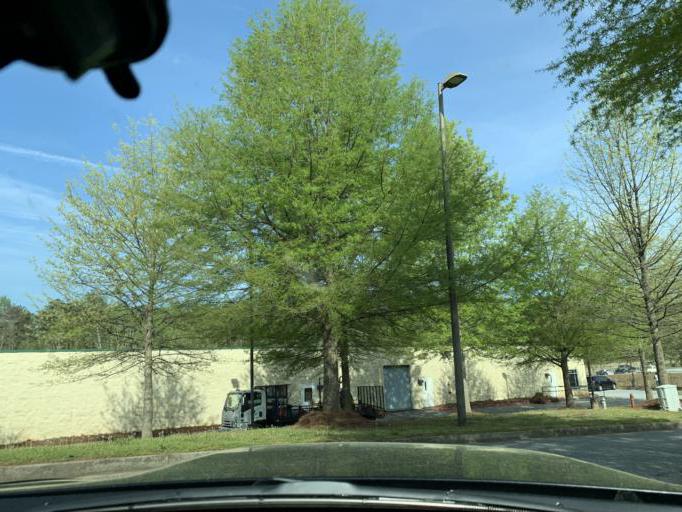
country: US
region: Georgia
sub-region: Forsyth County
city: Cumming
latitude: 34.2461
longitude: -84.1035
